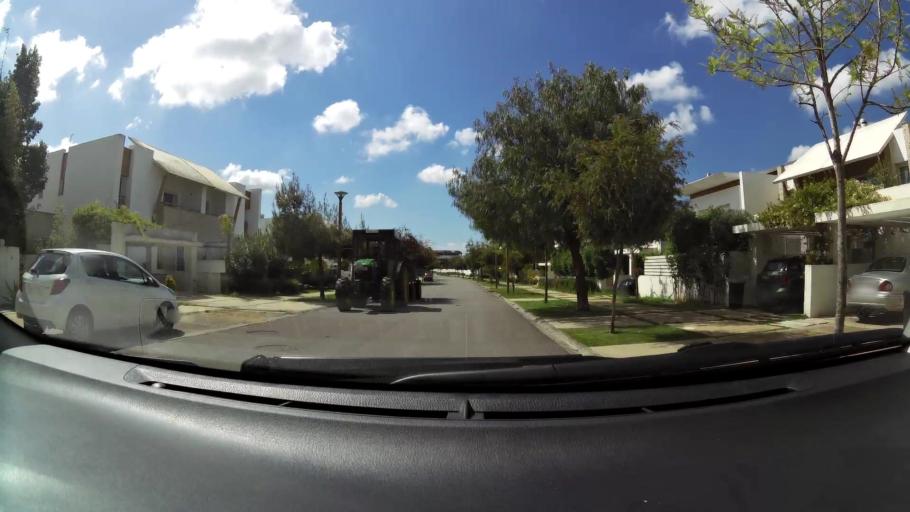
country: MA
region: Grand Casablanca
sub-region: Mediouna
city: Mediouna
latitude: 33.4909
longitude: -7.5858
